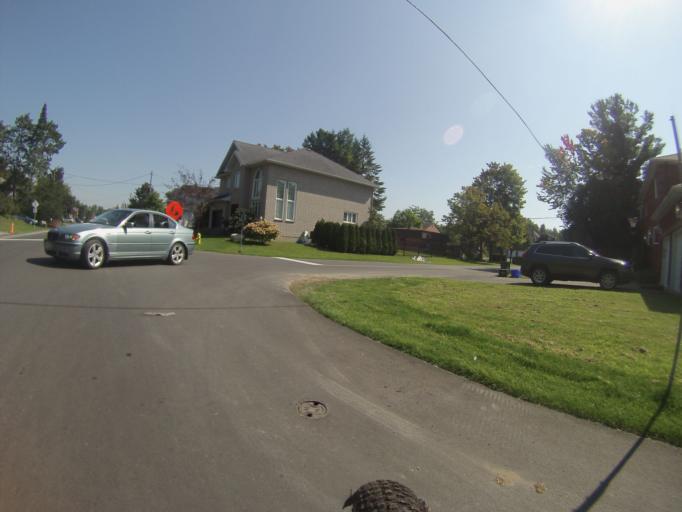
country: CA
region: Ontario
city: Ottawa
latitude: 45.3518
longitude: -75.6191
